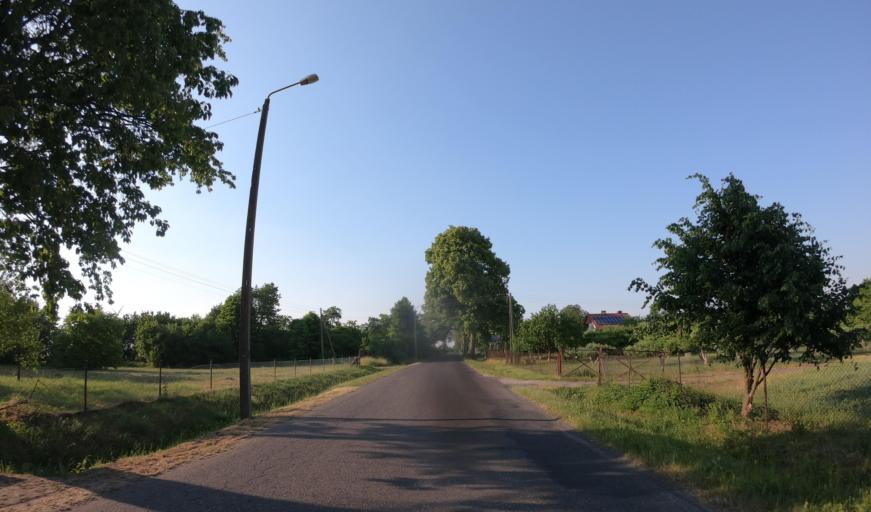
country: PL
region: West Pomeranian Voivodeship
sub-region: Powiat lobeski
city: Resko
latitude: 53.7465
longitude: 15.4099
